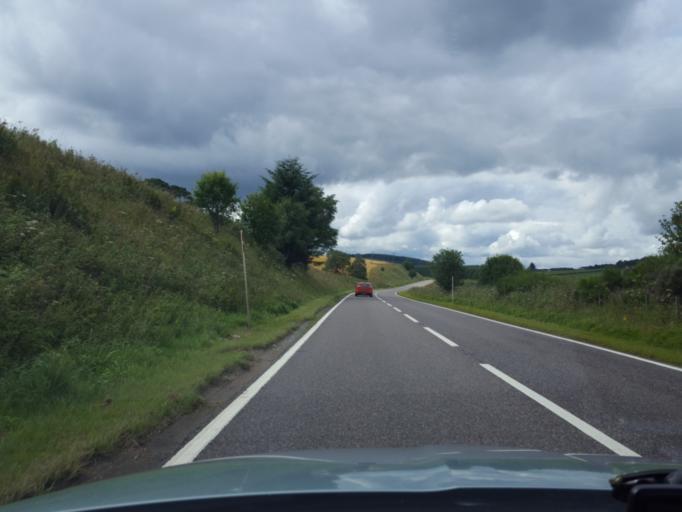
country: GB
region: Scotland
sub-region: Moray
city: Rothes
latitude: 57.4419
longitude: -3.2855
